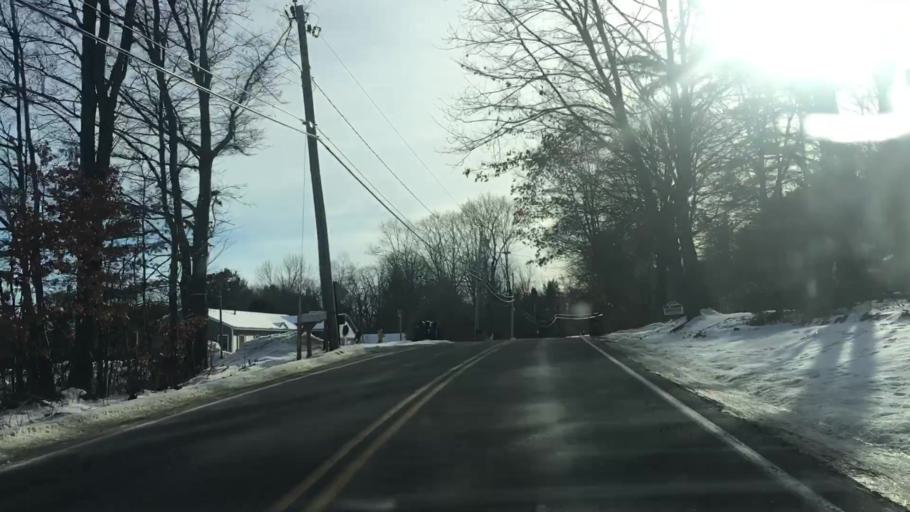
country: US
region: Maine
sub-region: Cumberland County
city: Westbrook
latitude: 43.7221
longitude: -70.3572
